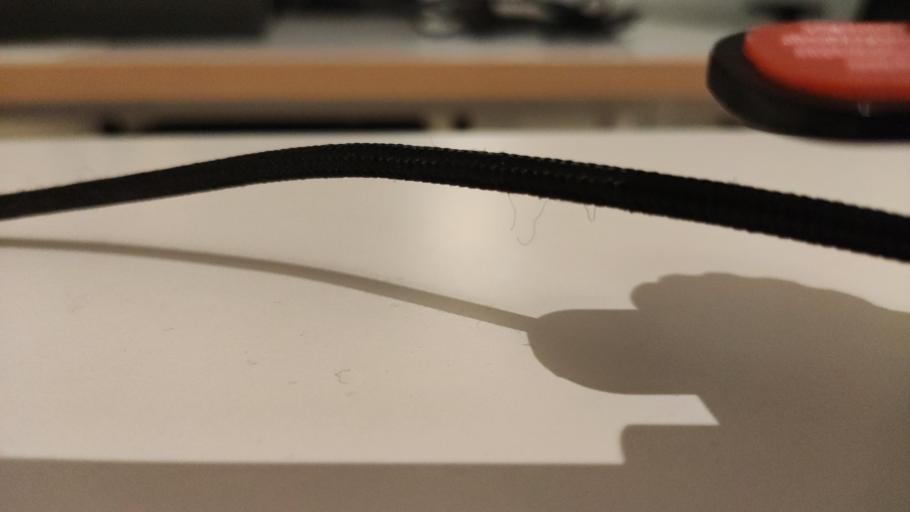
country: RU
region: Moskovskaya
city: Il'inskiy Pogost
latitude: 55.4976
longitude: 38.8741
